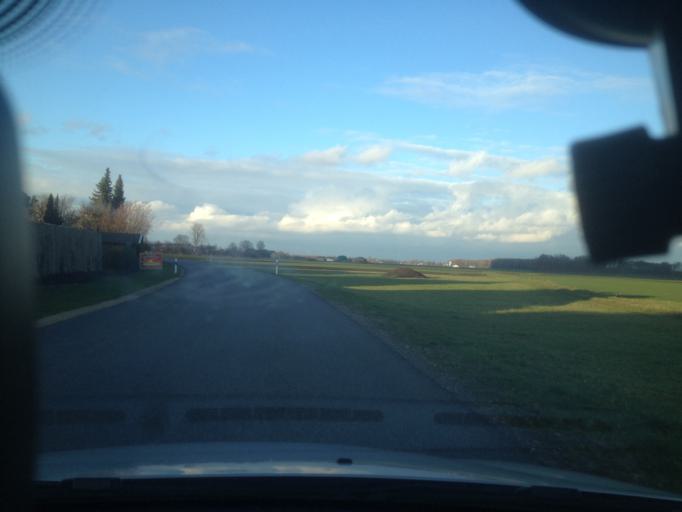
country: DE
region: Bavaria
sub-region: Upper Bavaria
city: Prittriching
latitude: 48.2065
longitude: 10.9325
